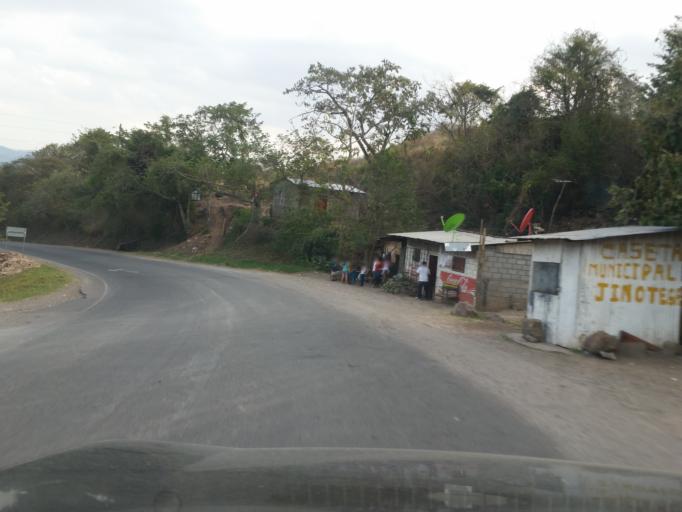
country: NI
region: Jinotega
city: San Rafael del Norte
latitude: 13.1681
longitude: -86.0661
